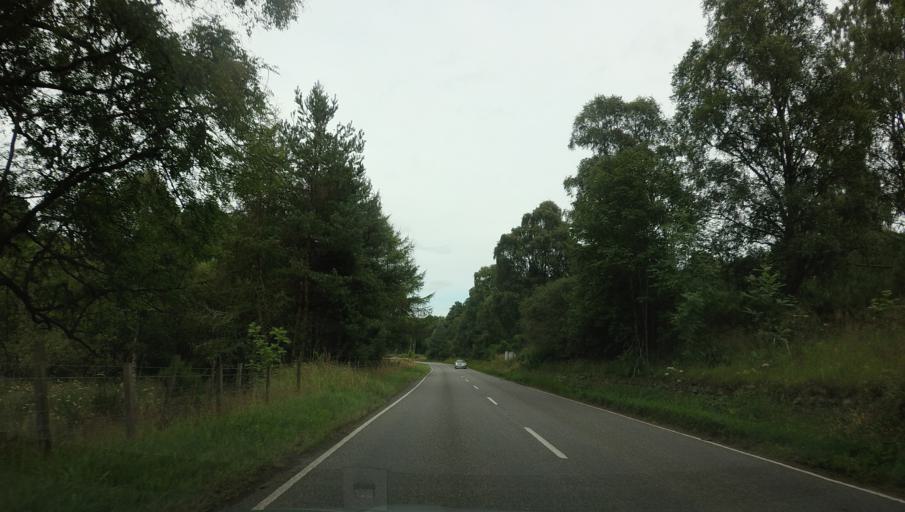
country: GB
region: Scotland
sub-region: Aberdeenshire
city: Aboyne
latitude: 57.0860
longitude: -2.7241
